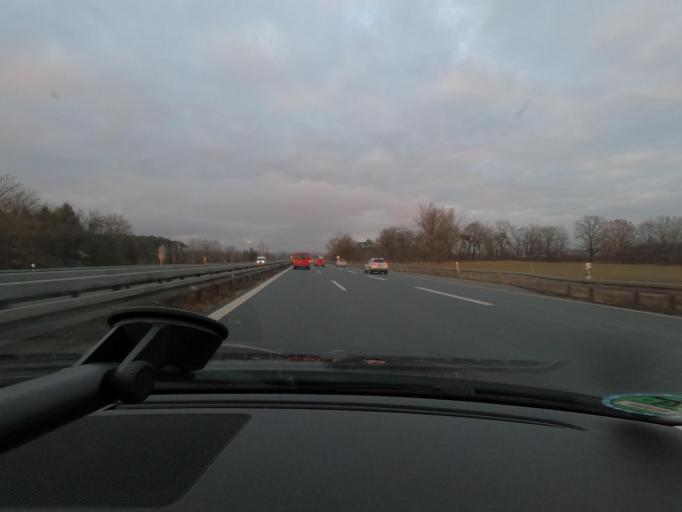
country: DE
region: Bavaria
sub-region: Upper Franconia
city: Hausen
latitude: 49.6801
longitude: 11.0526
